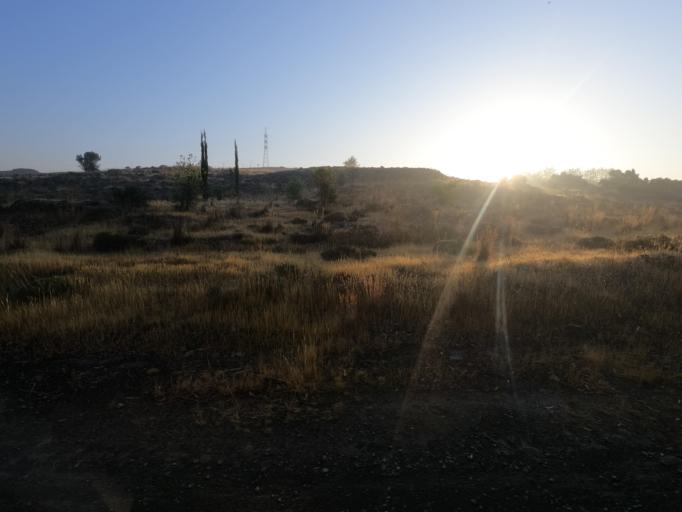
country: CY
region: Lefkosia
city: Alampra
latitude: 34.9776
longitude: 33.4168
